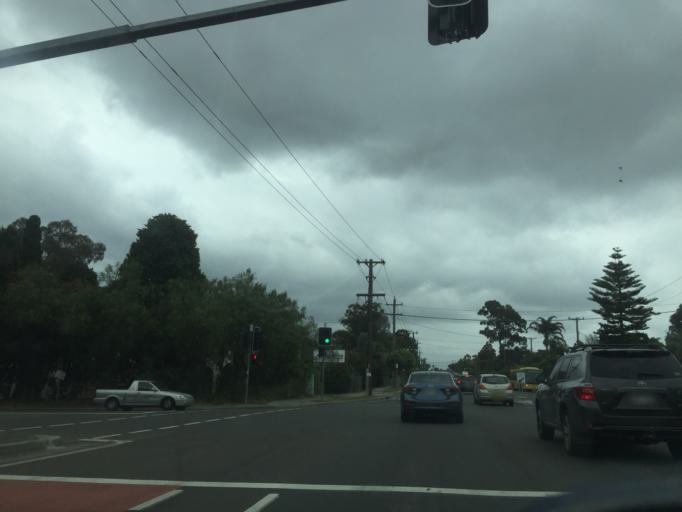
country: AU
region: New South Wales
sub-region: Holroyd
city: Girraween
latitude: -33.7669
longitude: 150.9519
